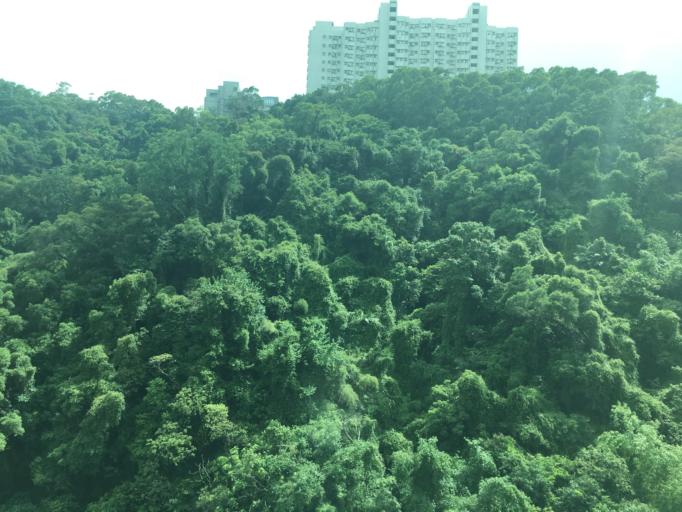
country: TW
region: Taipei
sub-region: Taipei
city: Banqiao
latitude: 25.0342
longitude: 121.3939
